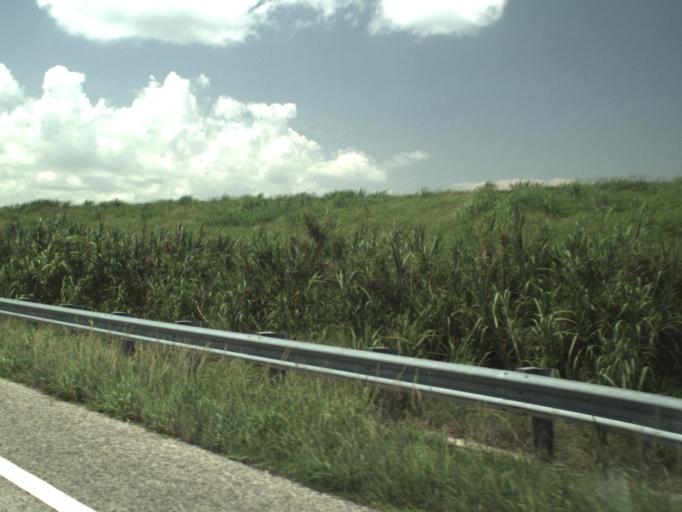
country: US
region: Florida
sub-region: Palm Beach County
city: South Bay
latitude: 26.6977
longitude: -80.7807
